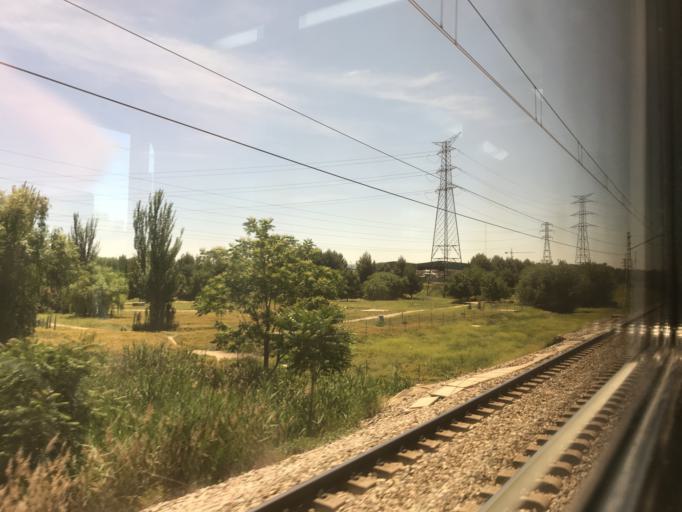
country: ES
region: Madrid
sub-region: Provincia de Madrid
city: Pinto
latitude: 40.2684
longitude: -3.7046
